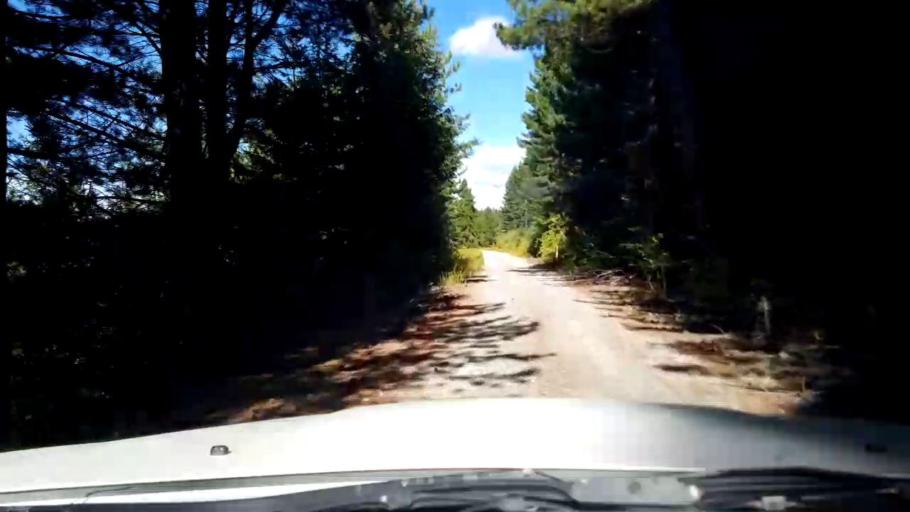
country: NZ
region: Canterbury
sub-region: Timaru District
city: Pleasant Point
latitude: -44.0129
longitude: 170.4663
